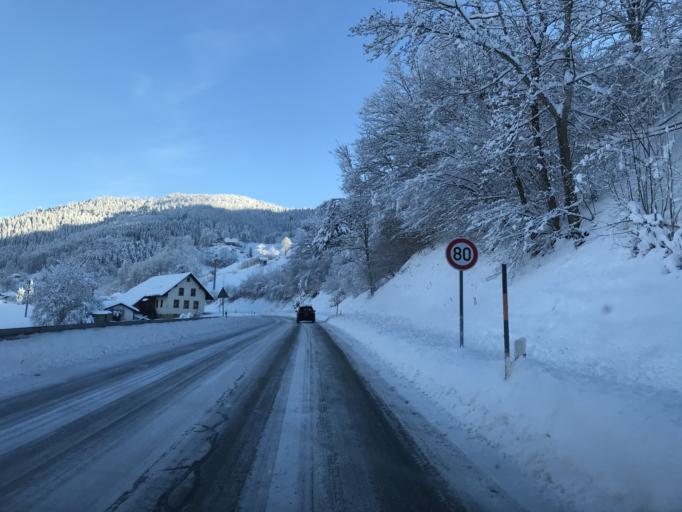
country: DE
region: Baden-Wuerttemberg
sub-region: Freiburg Region
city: Bollen
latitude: 47.7694
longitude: 7.8257
